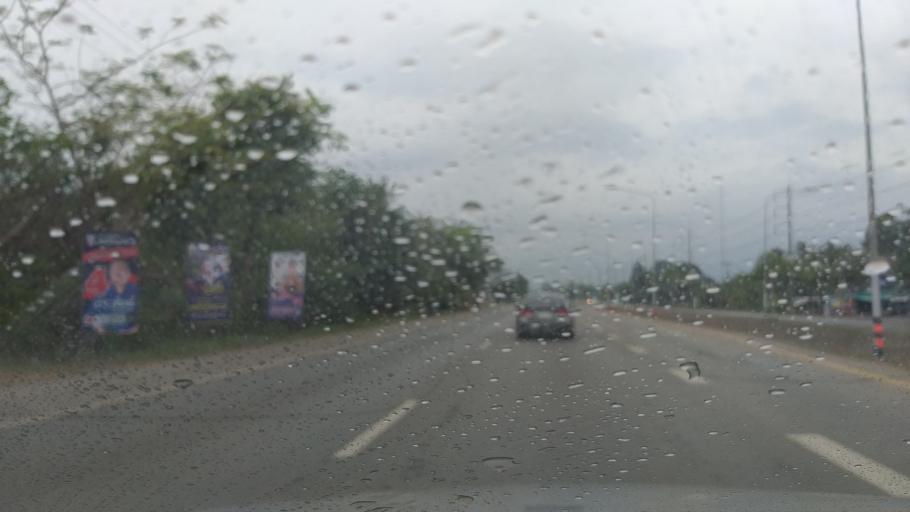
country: TH
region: Chanthaburi
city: Khlung
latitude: 12.4145
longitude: 102.3289
